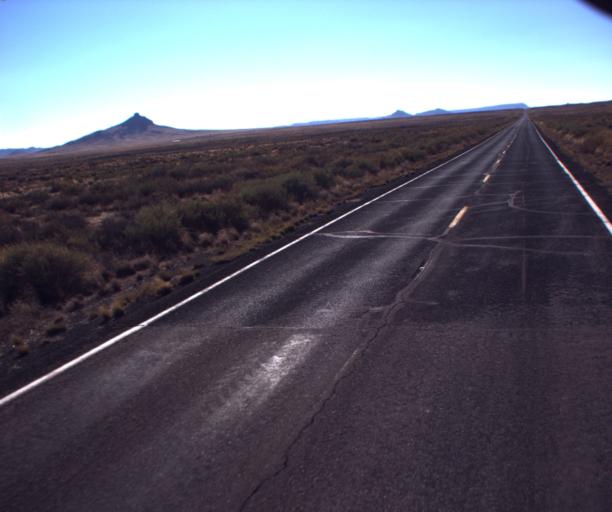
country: US
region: Arizona
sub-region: Navajo County
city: Dilkon
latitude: 35.5756
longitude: -110.4620
